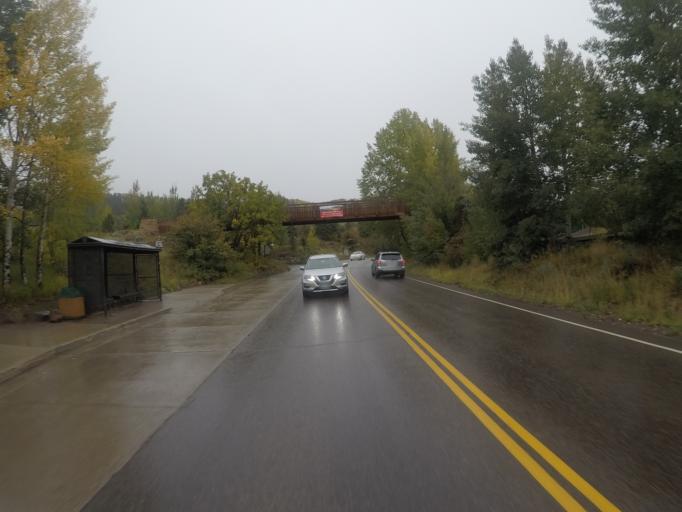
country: US
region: Colorado
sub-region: Pitkin County
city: Aspen
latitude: 39.1898
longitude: -106.8501
